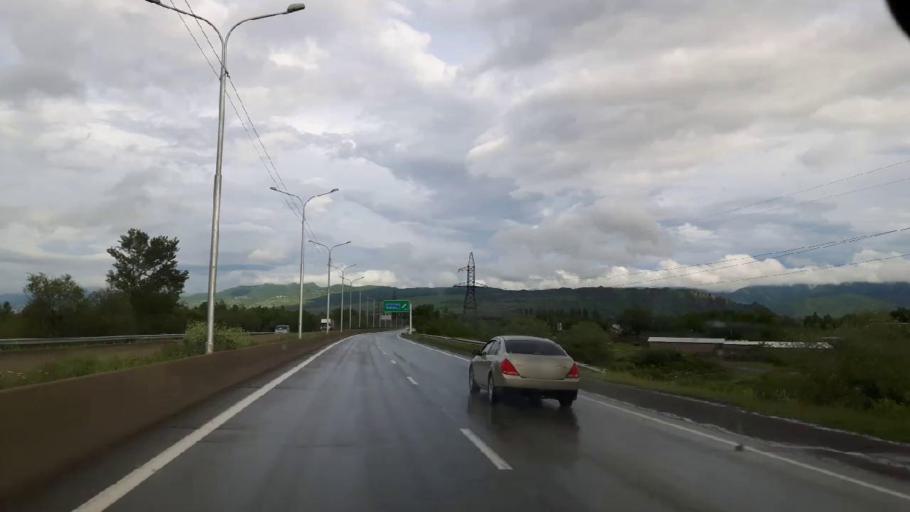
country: GE
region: Shida Kartli
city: Kaspi
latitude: 41.9175
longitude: 44.5524
